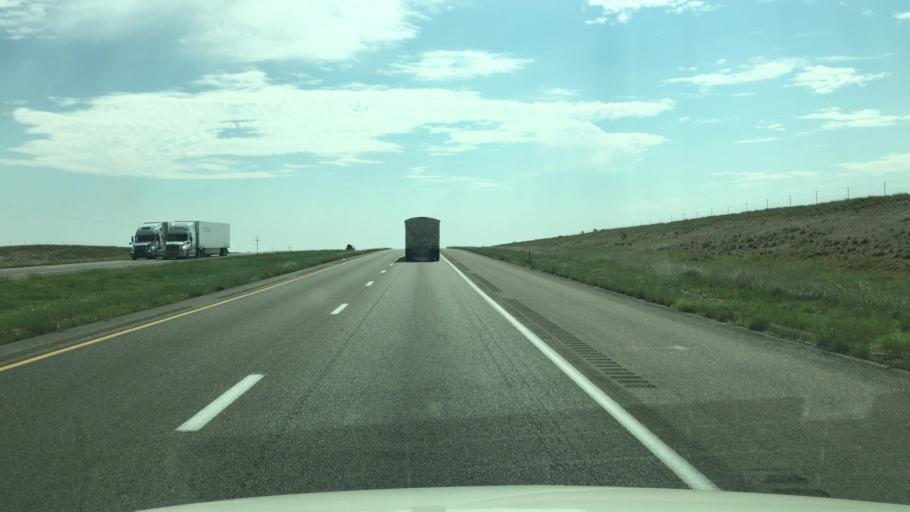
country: US
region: New Mexico
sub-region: Guadalupe County
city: Santa Rosa
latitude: 34.9819
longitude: -105.1027
